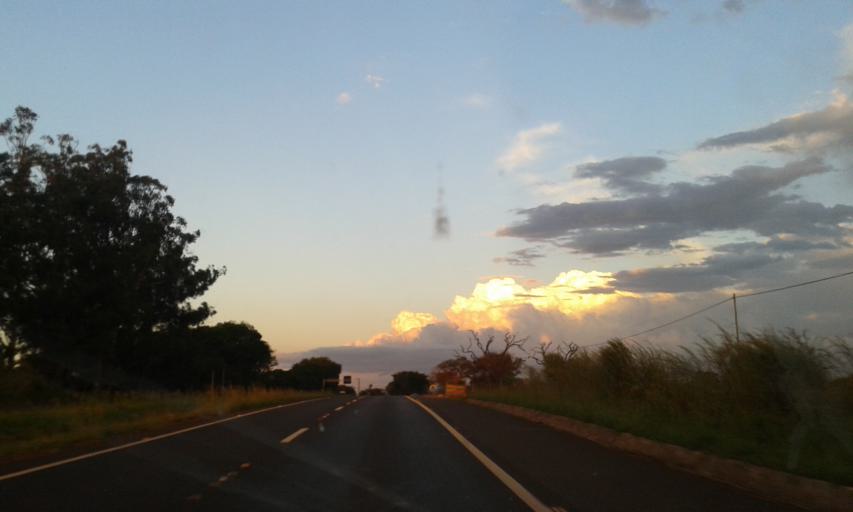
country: BR
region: Minas Gerais
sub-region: Monte Alegre De Minas
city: Monte Alegre de Minas
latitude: -18.8910
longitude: -48.6945
